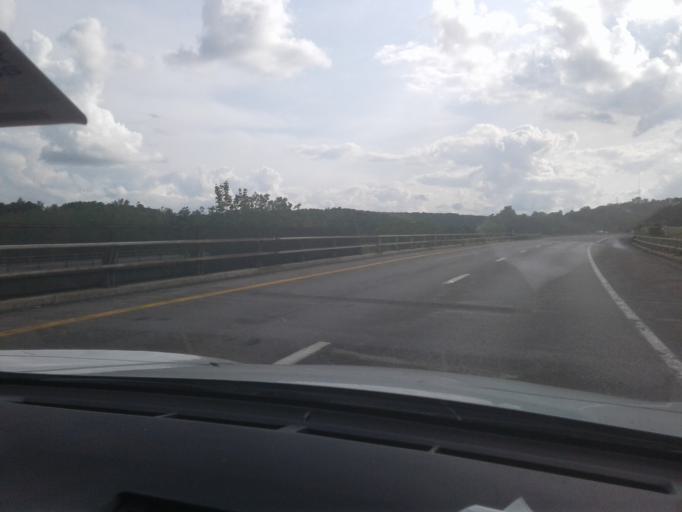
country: US
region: New York
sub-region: Onondaga County
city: East Syracuse
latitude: 43.0122
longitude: -76.0748
